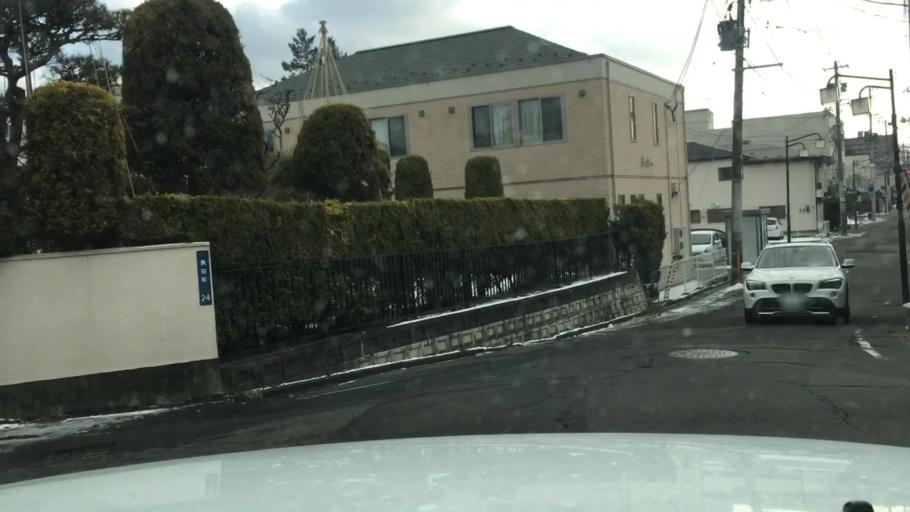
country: JP
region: Iwate
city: Morioka-shi
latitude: 39.7104
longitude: 141.1440
